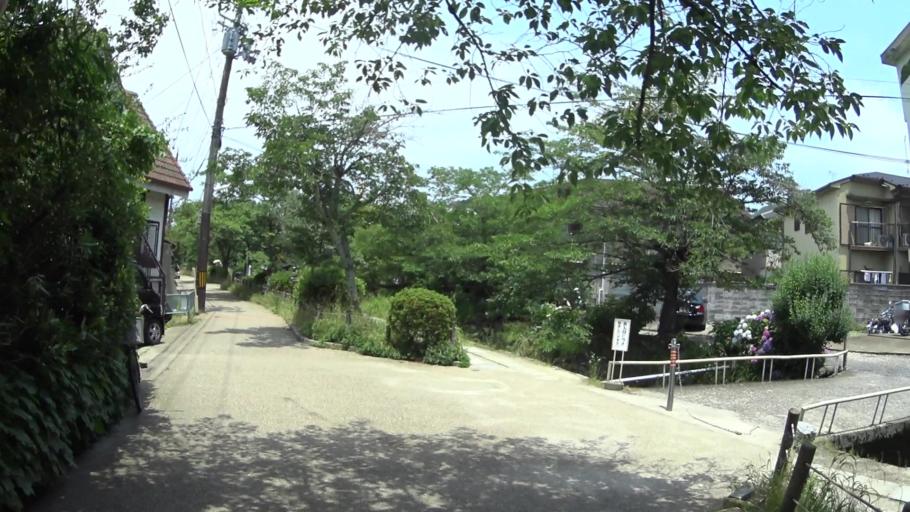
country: JP
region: Kyoto
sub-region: Kyoto-shi
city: Kamigyo-ku
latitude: 35.0247
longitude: 135.7964
